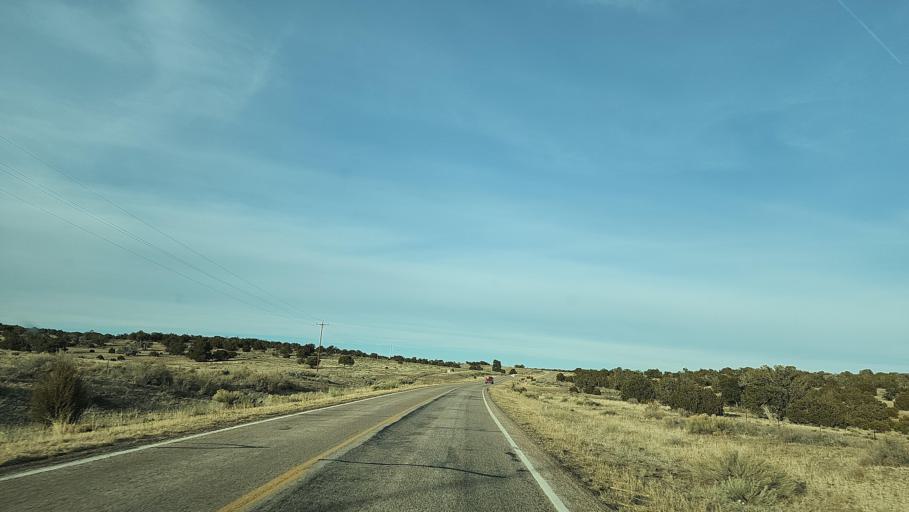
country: US
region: New Mexico
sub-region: Catron County
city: Reserve
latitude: 34.3835
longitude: -108.4557
